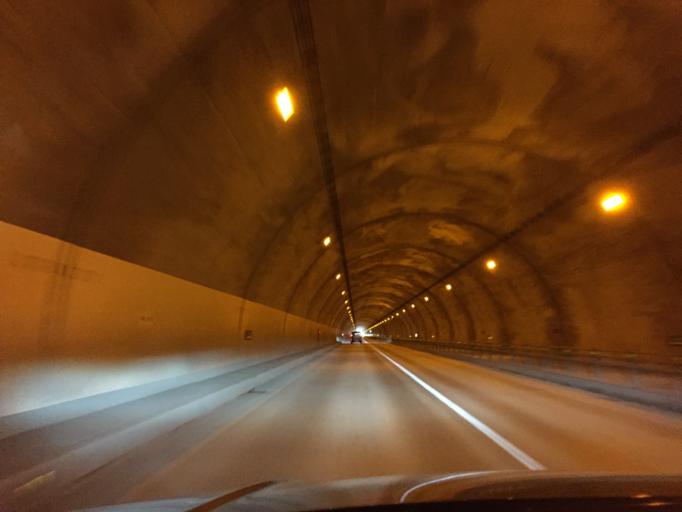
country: JP
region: Hokkaido
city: Utashinai
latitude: 43.5248
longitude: 142.0573
